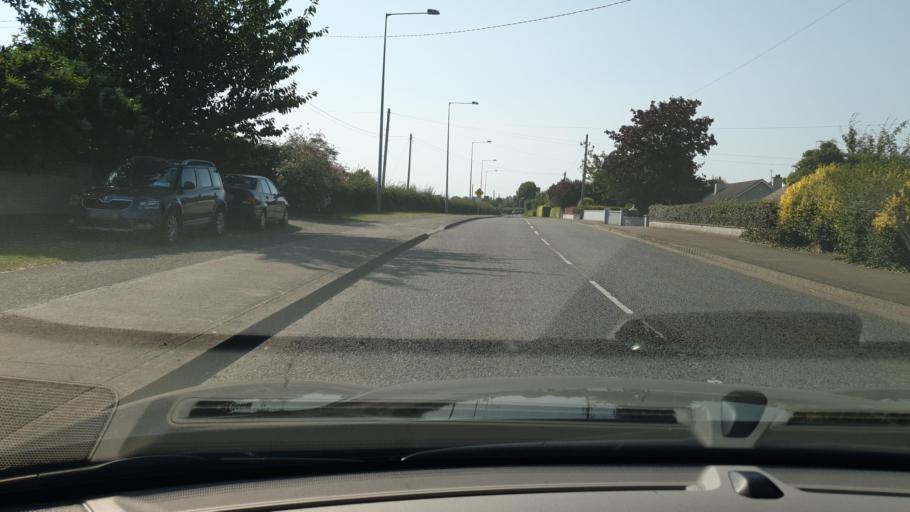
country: IE
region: Leinster
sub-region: An Mhi
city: Trim
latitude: 53.5643
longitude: -6.8040
